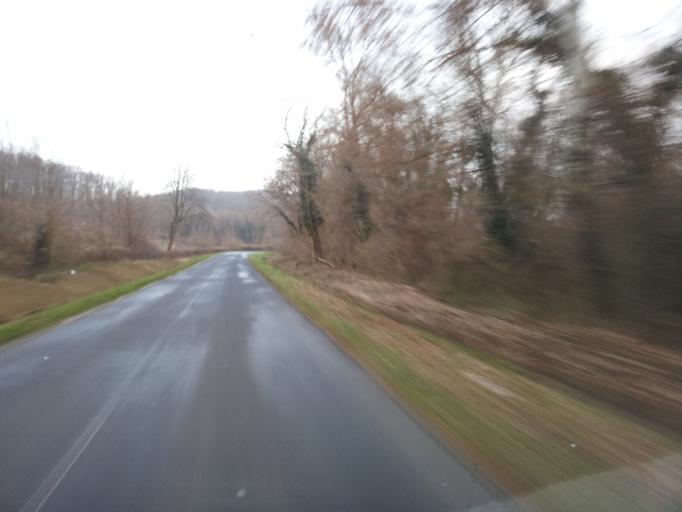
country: HU
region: Zala
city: Heviz
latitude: 46.8782
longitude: 17.1480
